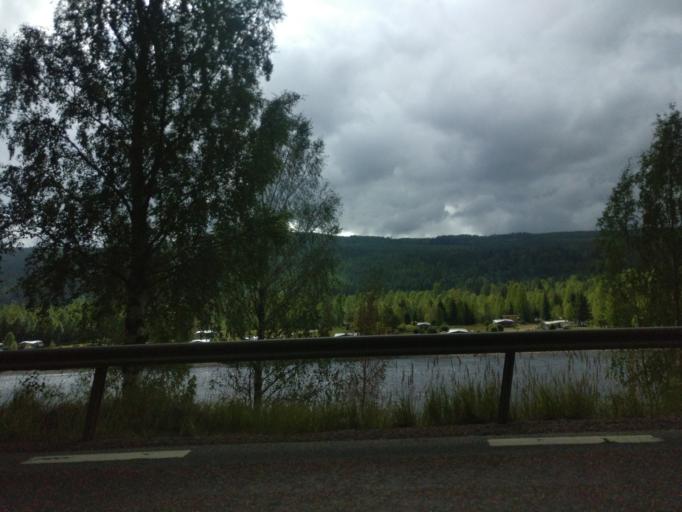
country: SE
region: Vaermland
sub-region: Torsby Kommun
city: Torsby
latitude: 60.7474
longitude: 12.8156
